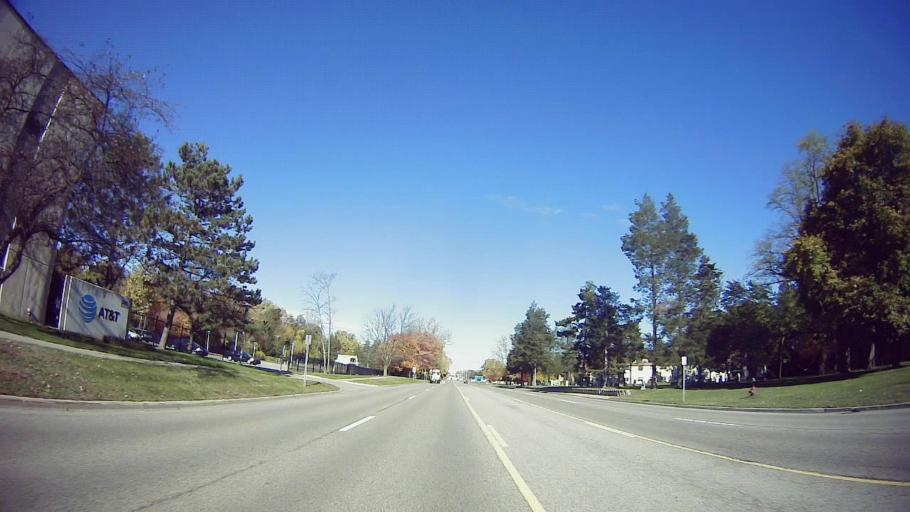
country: US
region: Michigan
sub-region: Oakland County
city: Southfield
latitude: 42.4744
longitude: -83.2609
